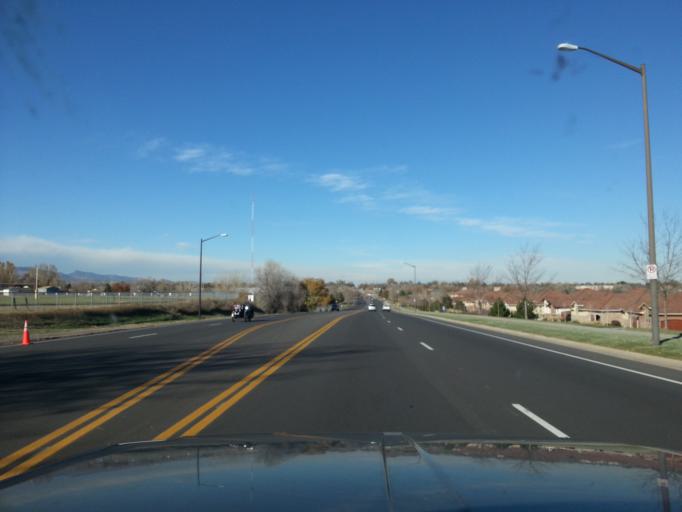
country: US
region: Colorado
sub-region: Larimer County
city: Loveland
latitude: 40.3864
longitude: -105.0971
